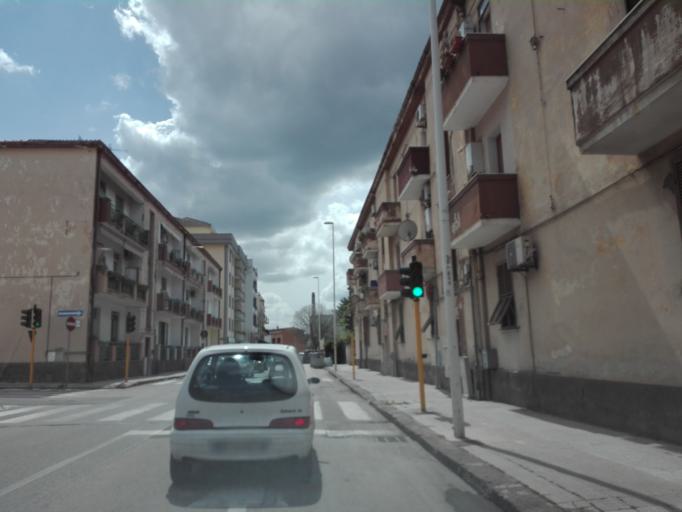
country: IT
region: Sardinia
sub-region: Provincia di Sassari
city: Sassari
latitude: 40.7350
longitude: 8.5565
